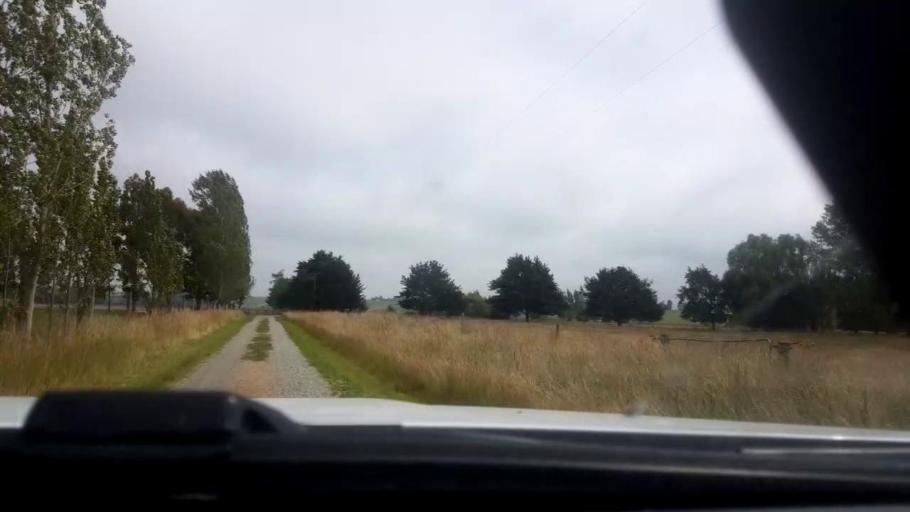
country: NZ
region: Canterbury
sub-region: Timaru District
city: Pleasant Point
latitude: -44.3240
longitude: 171.1939
